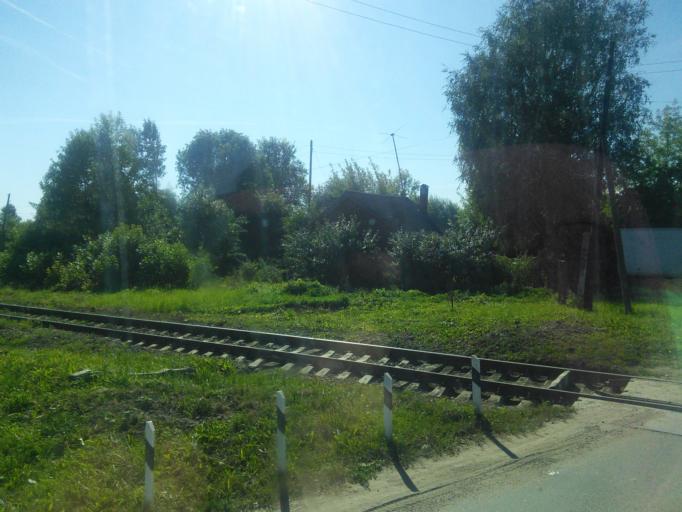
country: RU
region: Tverskaya
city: Kesova Gora
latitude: 57.5767
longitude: 37.3081
